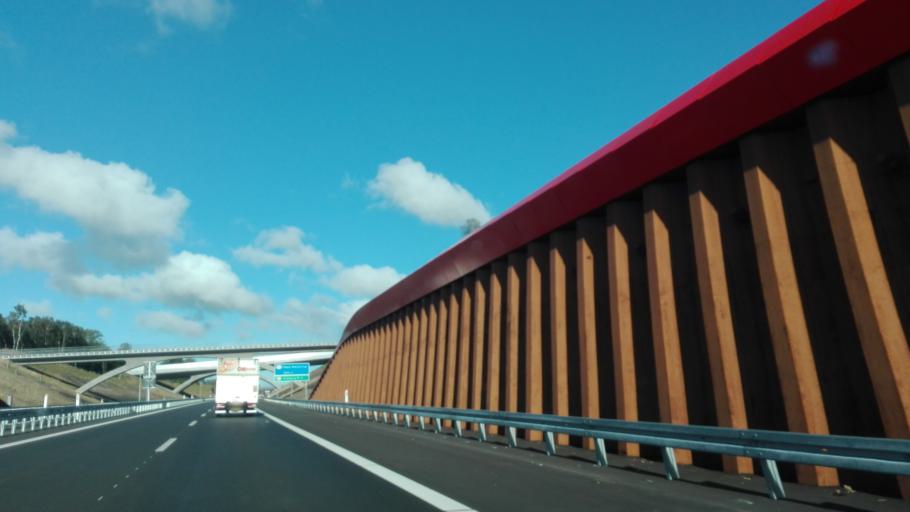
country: DK
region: Central Jutland
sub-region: Silkeborg Kommune
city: Silkeborg
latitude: 56.1901
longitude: 9.5687
